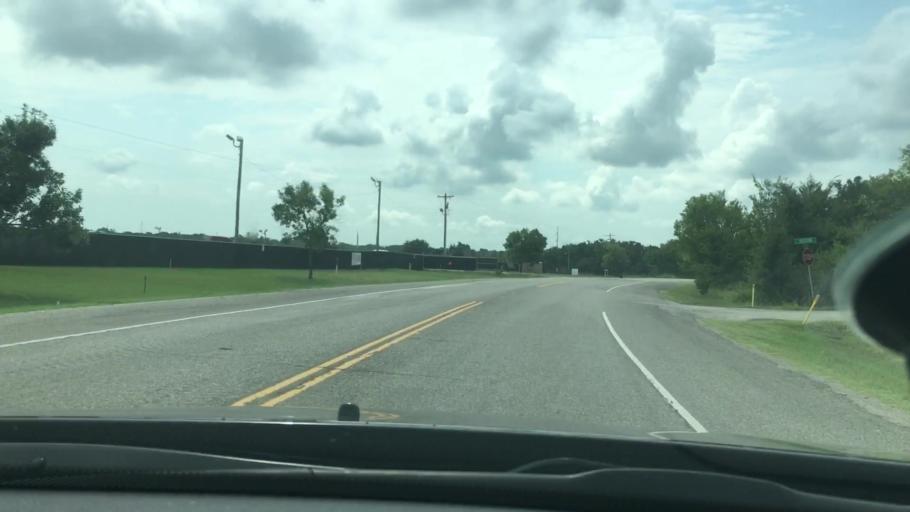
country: US
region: Oklahoma
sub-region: Carter County
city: Ardmore
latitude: 34.2002
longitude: -97.1085
